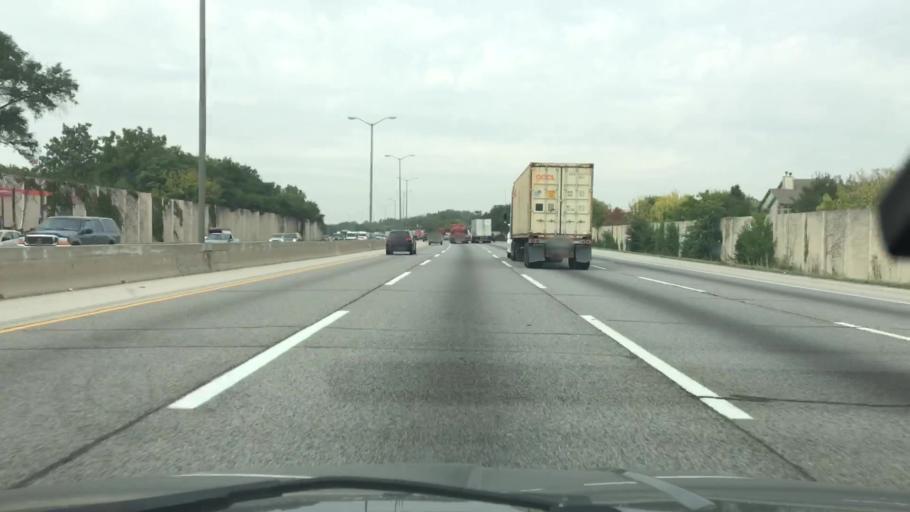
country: US
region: Illinois
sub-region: Cook County
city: Western Springs
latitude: 41.7944
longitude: -87.9080
